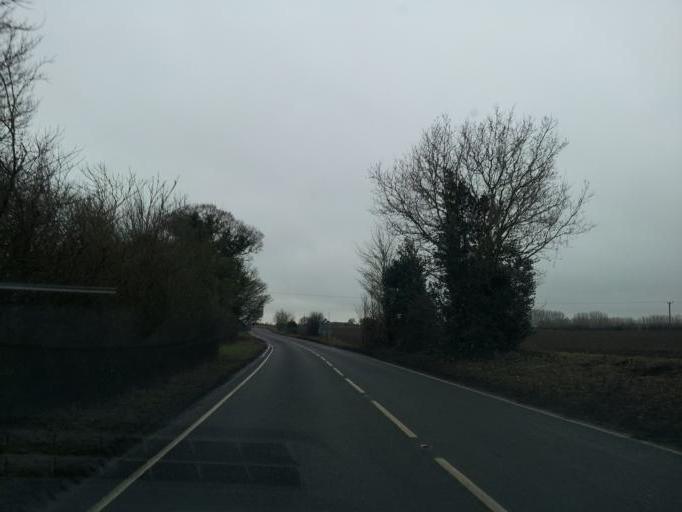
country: GB
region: England
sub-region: Essex
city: Manningtree
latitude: 51.9374
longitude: 1.0626
